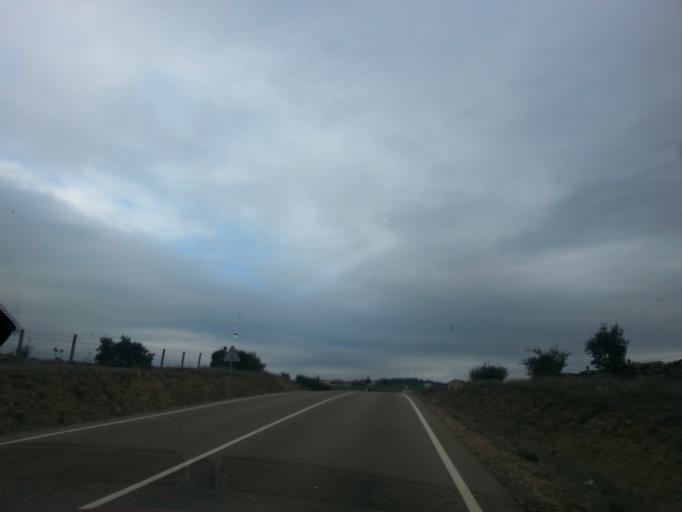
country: ES
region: Castille and Leon
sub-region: Provincia de Salamanca
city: Berrocal de Huebra
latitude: 40.7135
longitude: -6.0041
